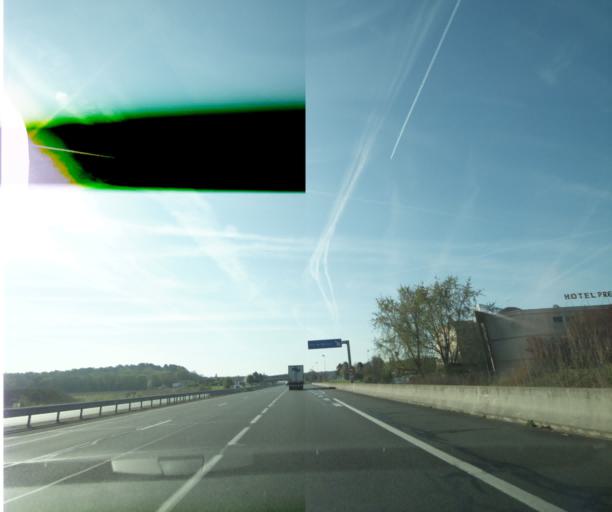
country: FR
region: Ile-de-France
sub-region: Departement de Seine-et-Marne
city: Nemours
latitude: 48.2674
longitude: 2.7186
